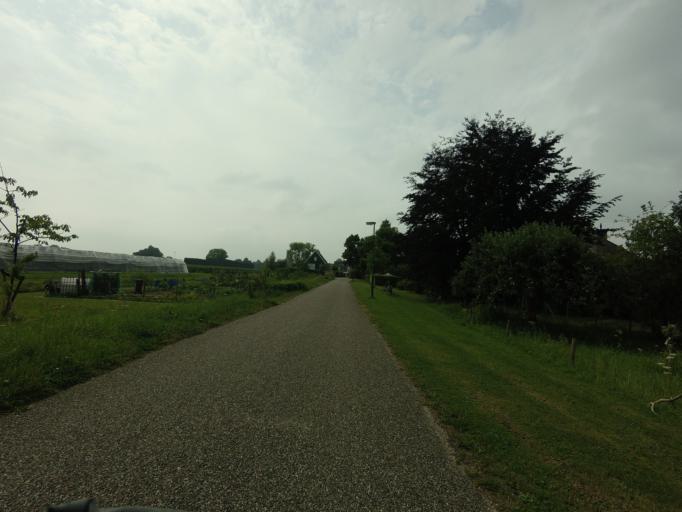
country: NL
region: Utrecht
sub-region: Gemeente Wijk bij Duurstede
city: Wijk bij Duurstede
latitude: 51.9780
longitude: 5.3500
